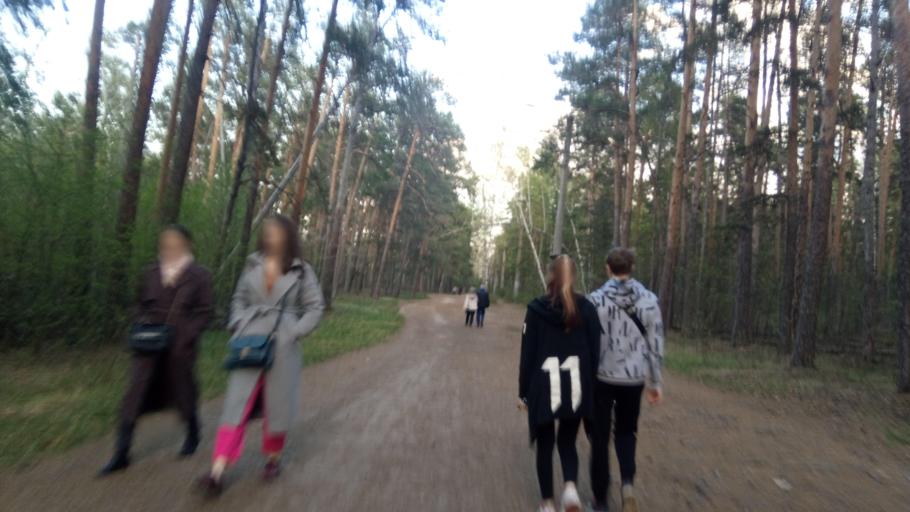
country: RU
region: Chelyabinsk
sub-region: Gorod Chelyabinsk
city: Chelyabinsk
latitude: 55.1663
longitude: 61.3503
